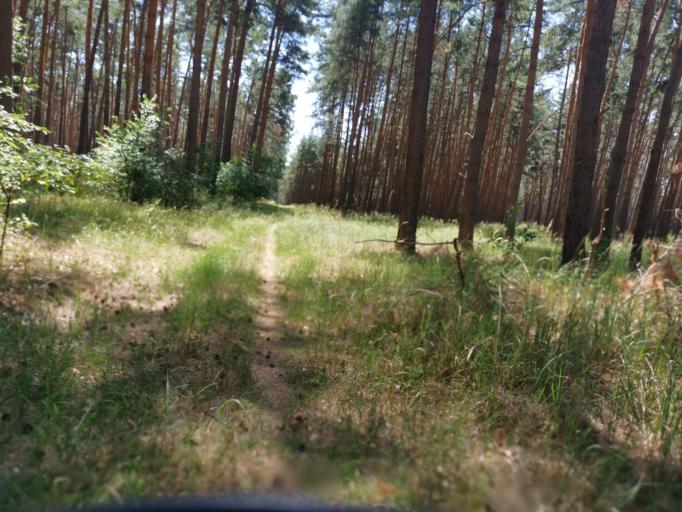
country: CZ
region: South Moravian
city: Bzenec
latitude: 48.9251
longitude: 17.2456
